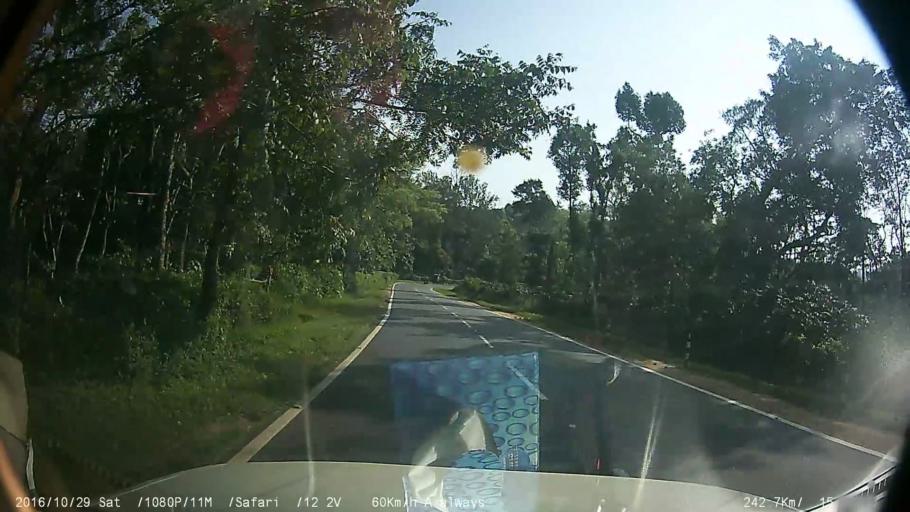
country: IN
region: Karnataka
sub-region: Kodagu
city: Suntikoppa
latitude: 12.4362
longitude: 75.7872
